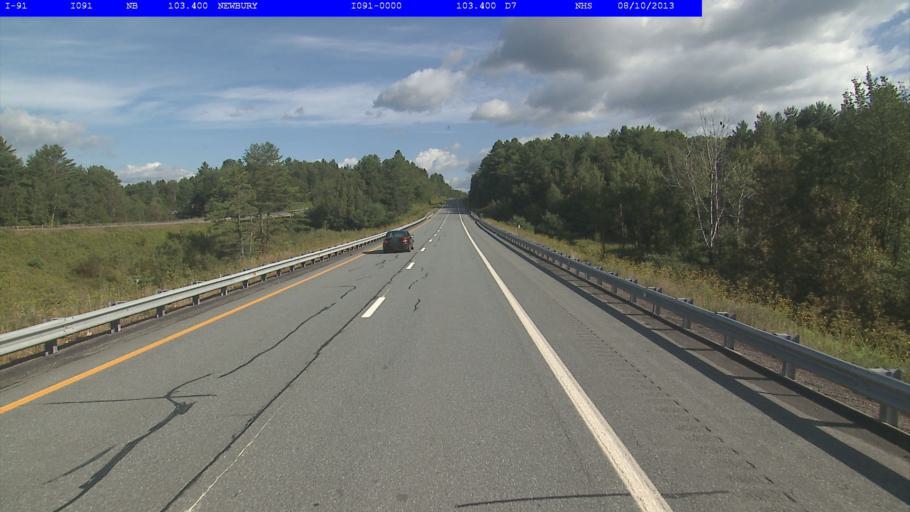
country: US
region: New Hampshire
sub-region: Grafton County
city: Haverhill
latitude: 44.0624
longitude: -72.1087
